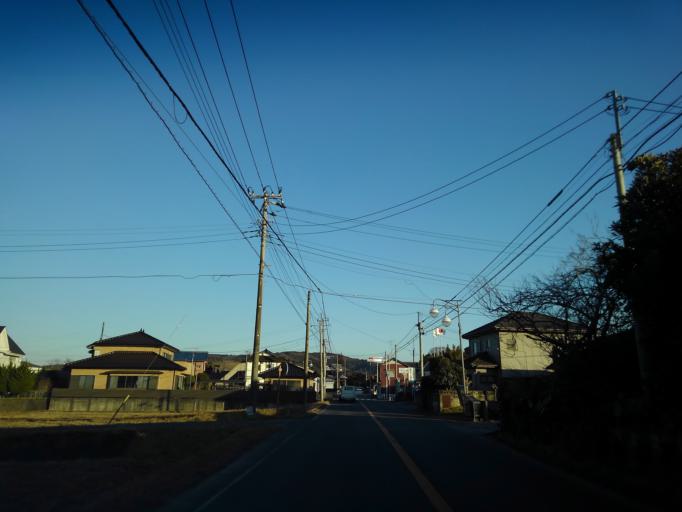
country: JP
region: Chiba
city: Kimitsu
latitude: 35.2990
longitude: 139.9765
